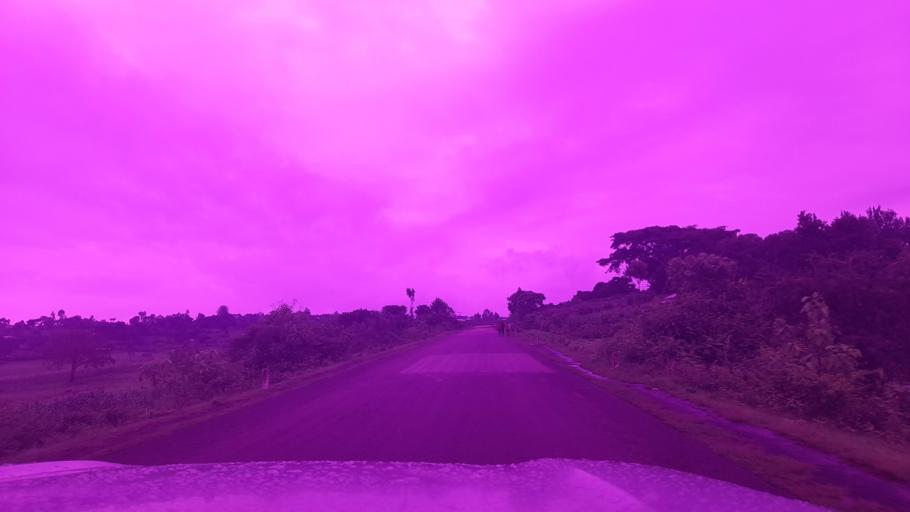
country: ET
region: Oromiya
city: Jima
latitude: 7.7299
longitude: 37.2665
